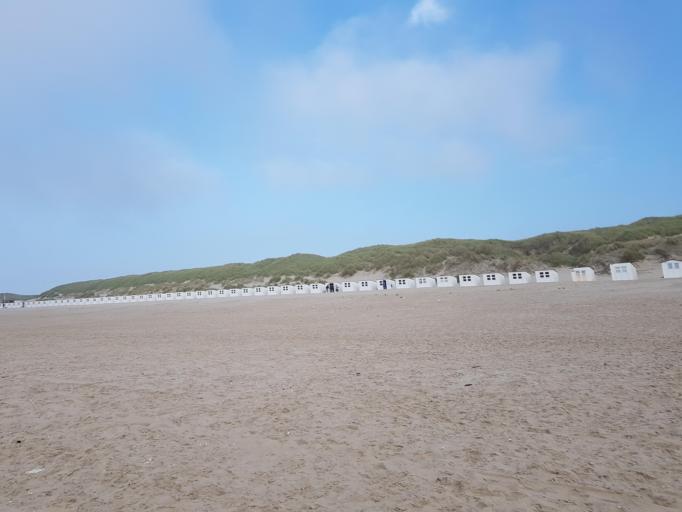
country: NL
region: North Holland
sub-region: Gemeente Texel
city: Den Burg
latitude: 53.1607
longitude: 4.8168
